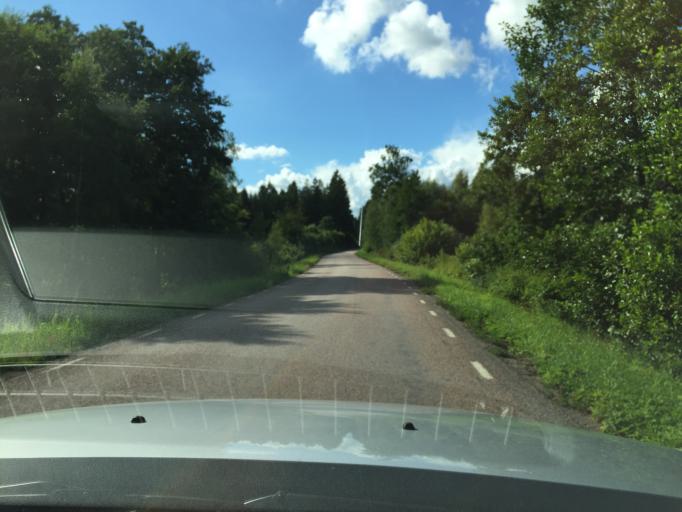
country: SE
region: Skane
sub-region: Hassleholms Kommun
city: Tormestorp
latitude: 56.0029
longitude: 13.7995
